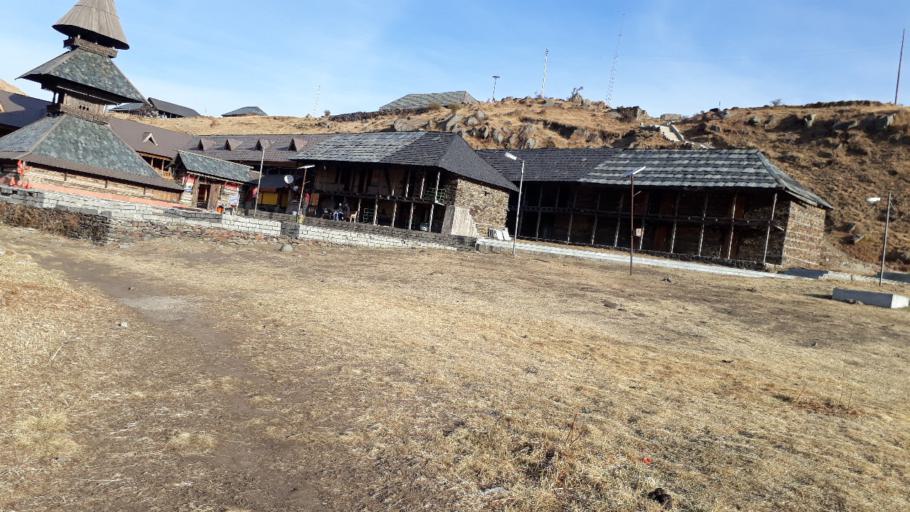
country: IN
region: Himachal Pradesh
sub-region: Mandi
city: Pandoh
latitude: 31.7544
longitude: 77.1018
